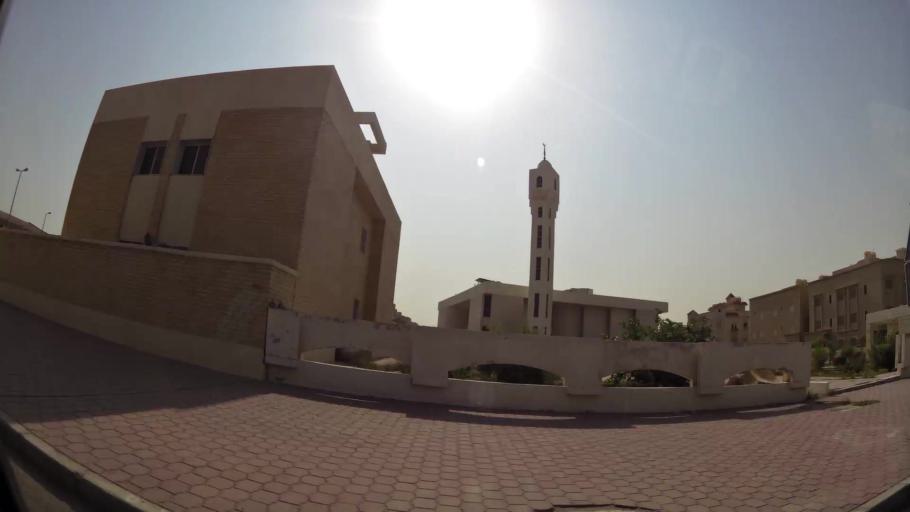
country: KW
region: Muhafazat al Jahra'
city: Al Jahra'
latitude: 29.3373
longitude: 47.7660
